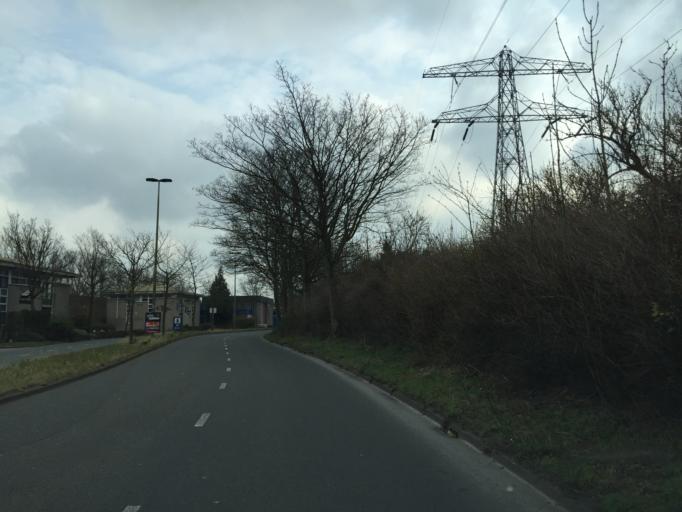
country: NL
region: South Holland
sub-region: Gemeente Delft
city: Delft
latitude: 51.9877
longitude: 4.3656
